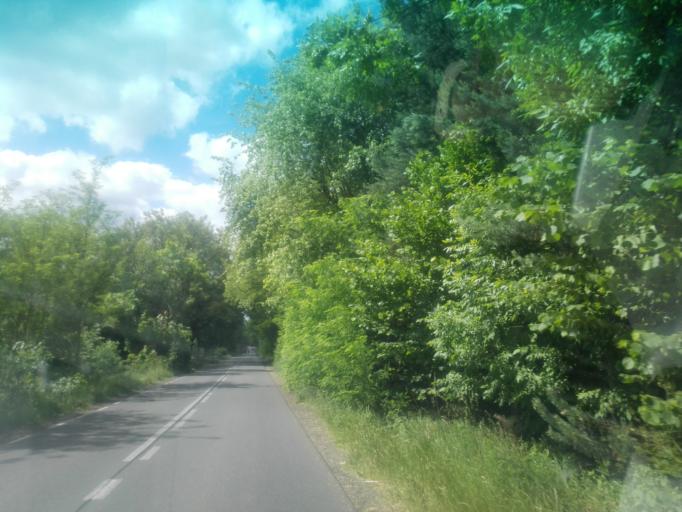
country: PL
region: Silesian Voivodeship
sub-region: Powiat czestochowski
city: Olsztyn
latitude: 50.7636
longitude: 19.2724
